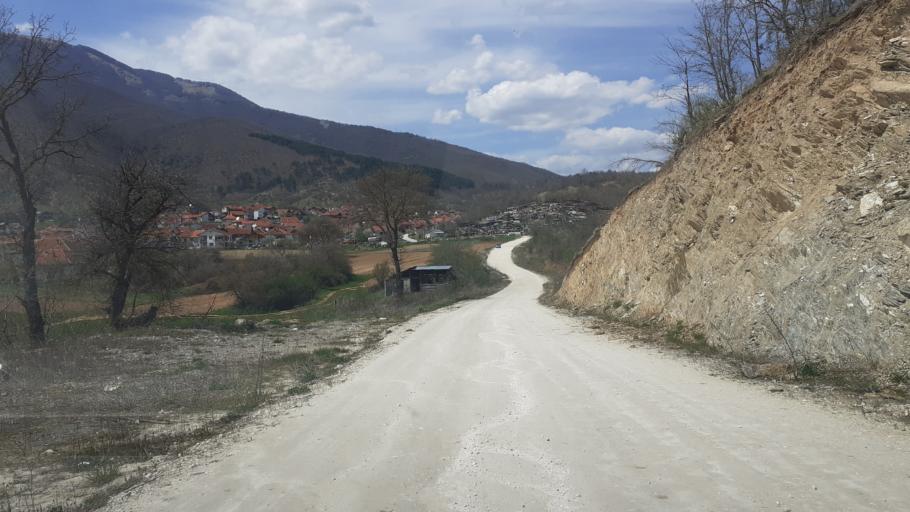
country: MK
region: Makedonski Brod
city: Makedonski Brod
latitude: 41.5145
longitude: 21.2229
